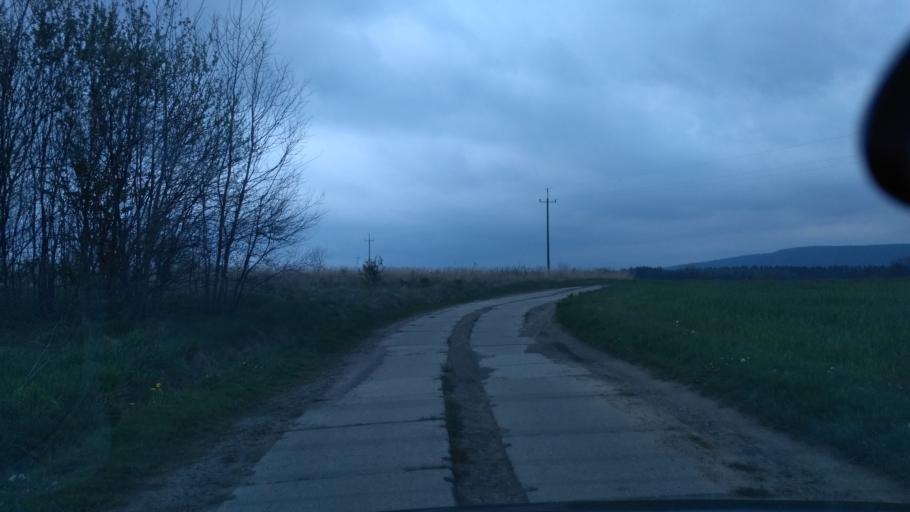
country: PL
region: Subcarpathian Voivodeship
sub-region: Powiat brzozowski
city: Dydnia
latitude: 49.6474
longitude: 22.2681
